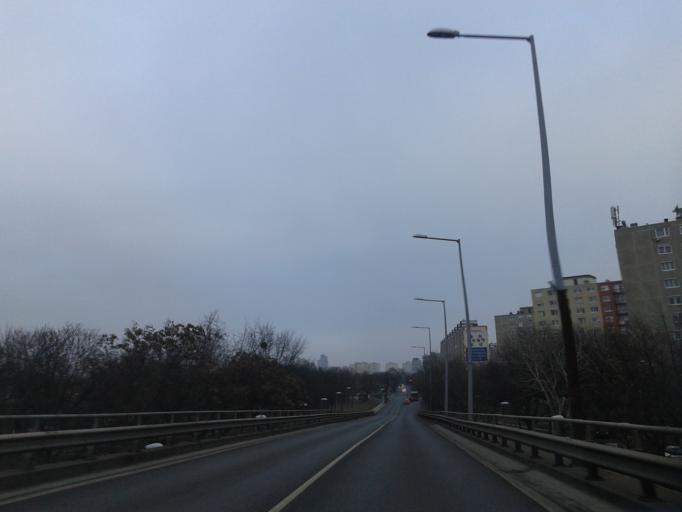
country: HU
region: Budapest
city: Budapest XIV. keruelet
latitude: 47.5318
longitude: 19.1281
